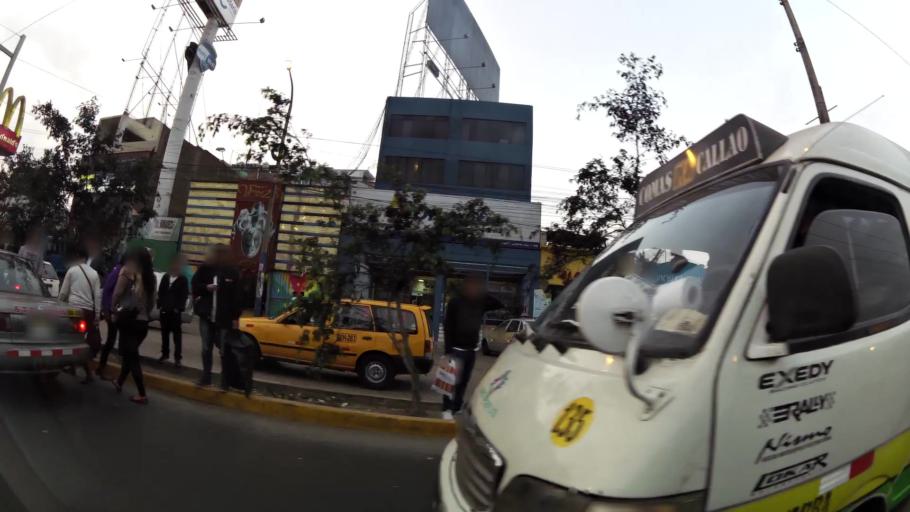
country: PE
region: Callao
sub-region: Callao
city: Callao
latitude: -12.0783
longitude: -77.0803
